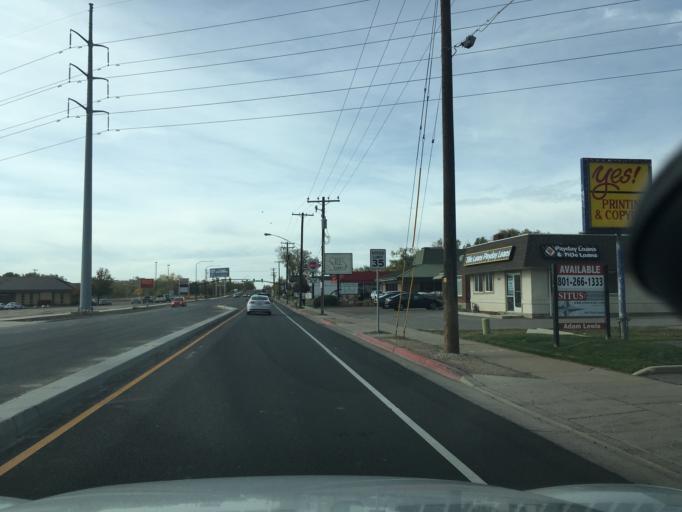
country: US
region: Utah
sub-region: Davis County
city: Layton
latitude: 41.0602
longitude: -111.9586
